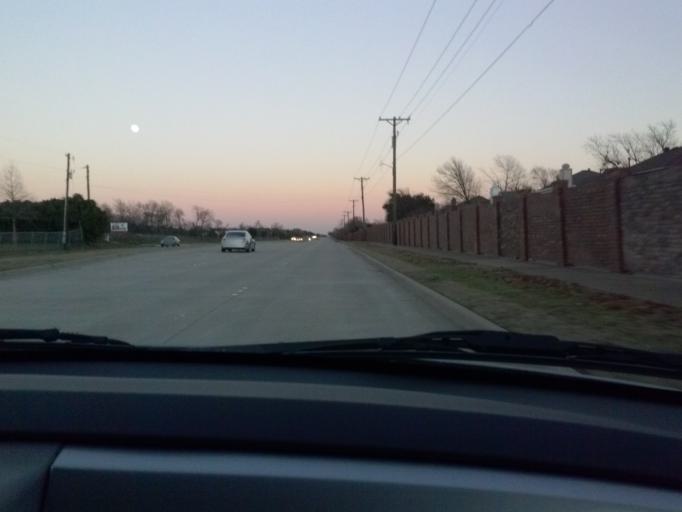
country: US
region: Texas
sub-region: Collin County
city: Allen
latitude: 33.0860
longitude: -96.7288
